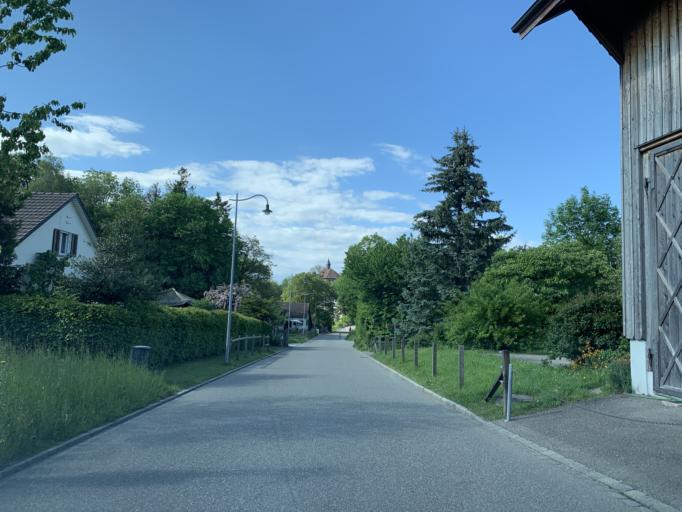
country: CH
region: Zurich
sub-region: Bezirk Winterthur
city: Kollbrunn / Kollbrunn (Dorfkern)
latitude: 47.4545
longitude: 8.7434
